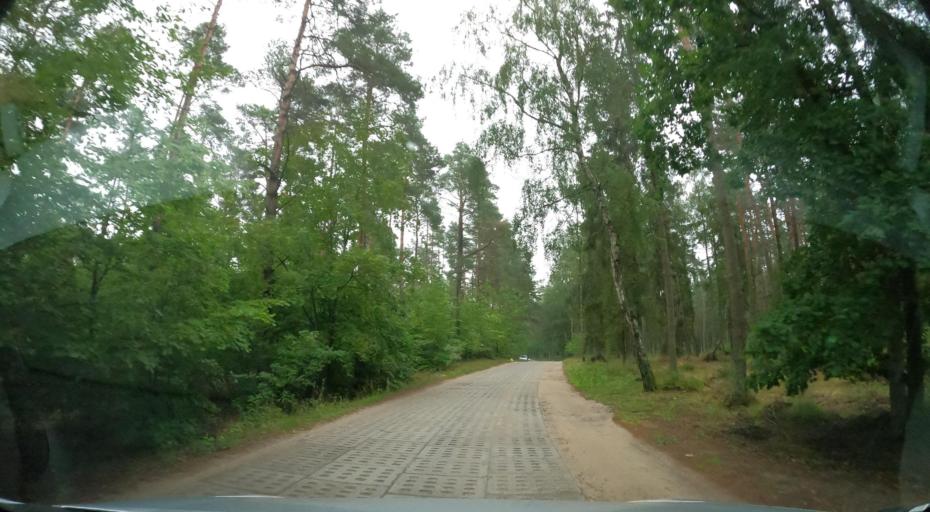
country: PL
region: Pomeranian Voivodeship
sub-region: Powiat kartuski
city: Chwaszczyno
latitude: 54.4195
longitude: 18.4256
